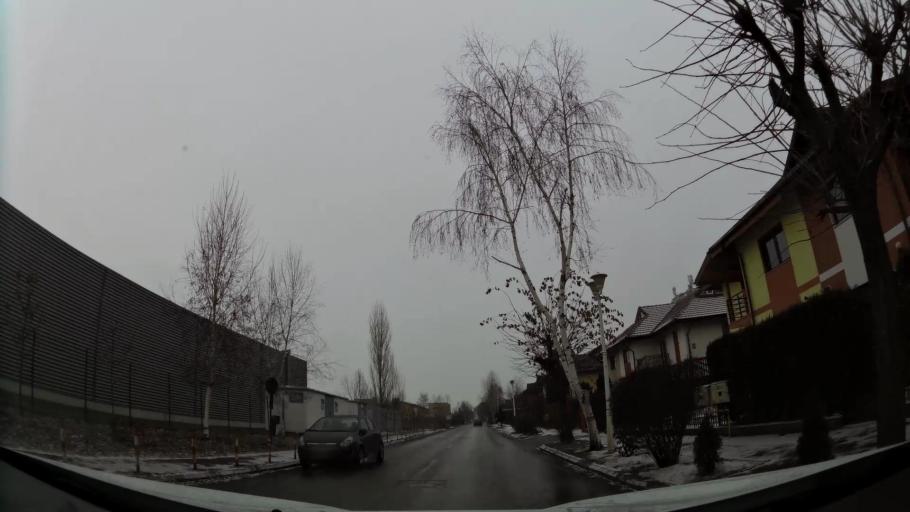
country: RO
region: Prahova
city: Ploiesti
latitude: 44.9563
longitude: 25.9948
